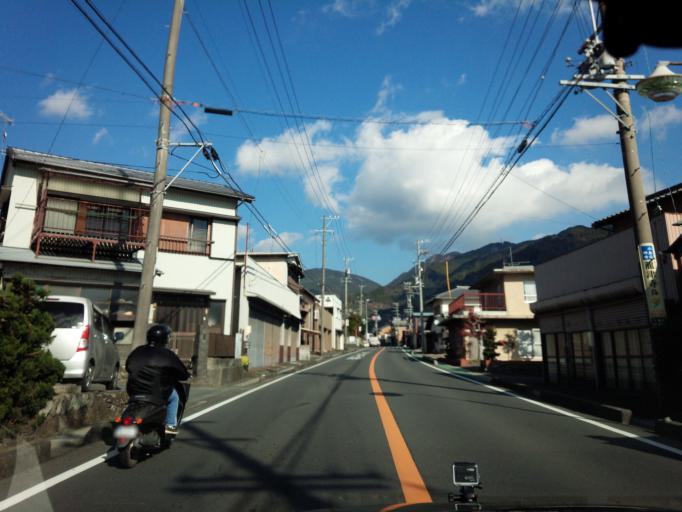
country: JP
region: Shizuoka
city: Fujinomiya
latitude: 35.0884
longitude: 138.5158
